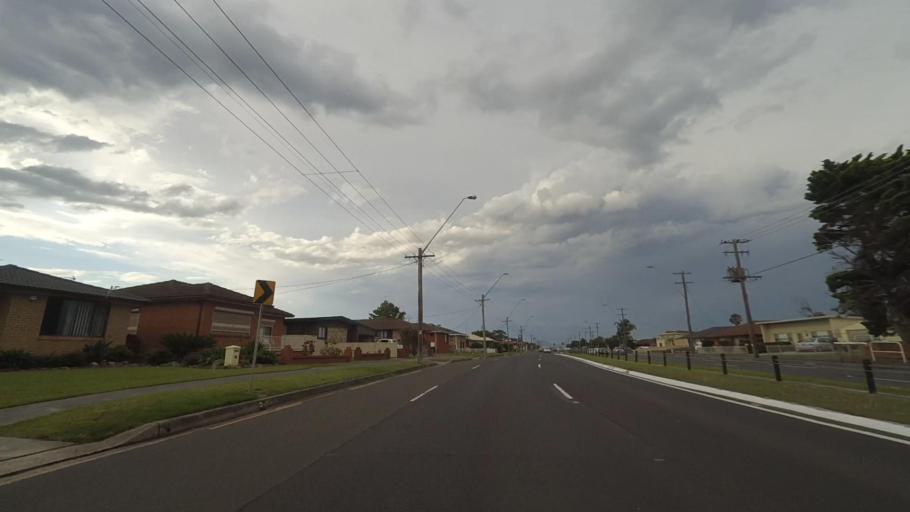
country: AU
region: New South Wales
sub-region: Shellharbour
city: Barrack Heights
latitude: -34.5669
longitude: 150.8602
